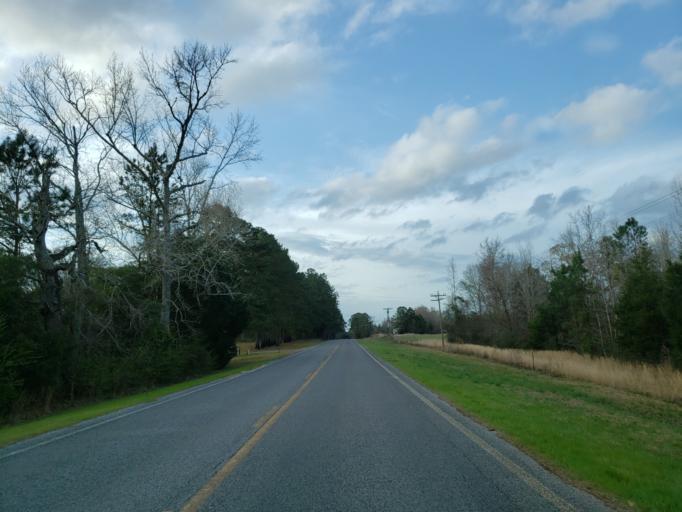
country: US
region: Mississippi
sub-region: Clarke County
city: Stonewall
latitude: 32.1872
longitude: -88.6788
